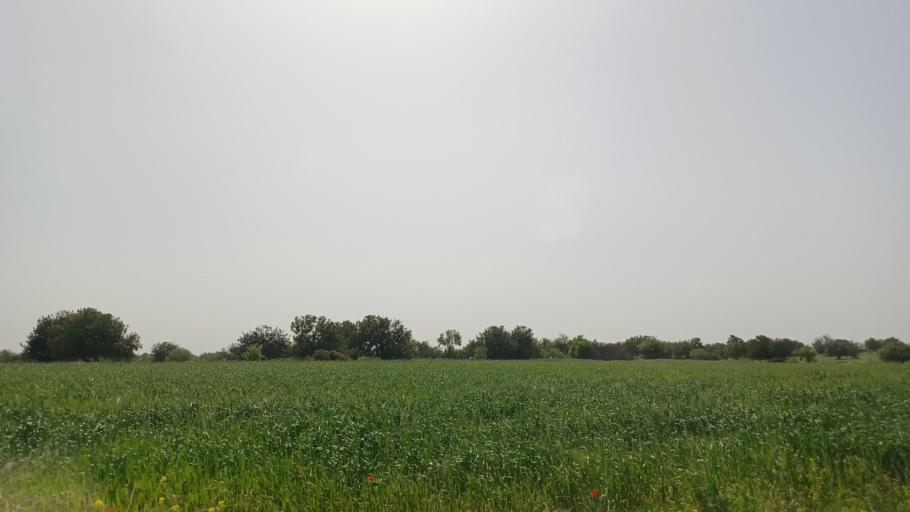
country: CY
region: Limassol
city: Pissouri
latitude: 34.7304
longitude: 32.7304
